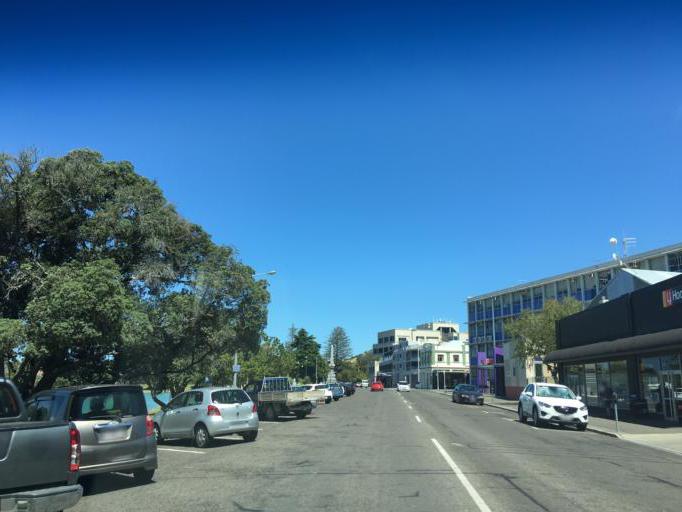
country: NZ
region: Gisborne
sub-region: Gisborne District
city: Gisborne
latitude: -38.6657
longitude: 178.0274
